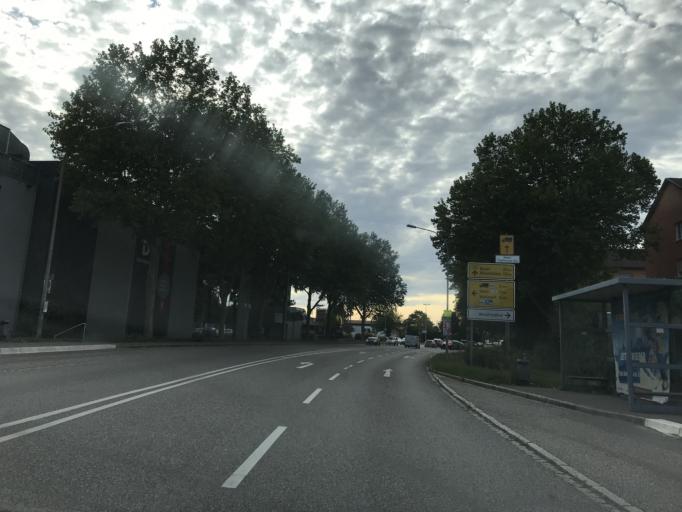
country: DE
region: Baden-Wuerttemberg
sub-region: Freiburg Region
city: Bad Sackingen
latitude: 47.5541
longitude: 7.9323
